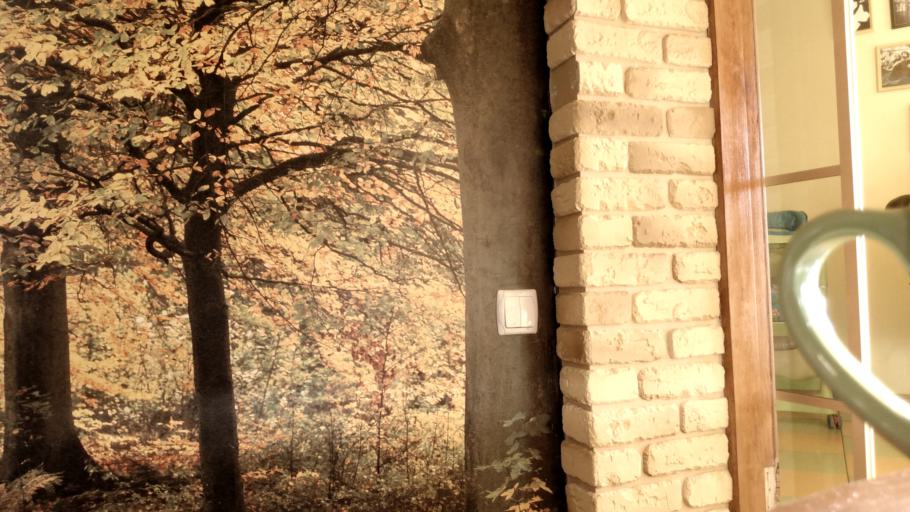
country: RU
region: Vologda
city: Imeni Zhelyabova
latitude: 58.8234
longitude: 36.8742
